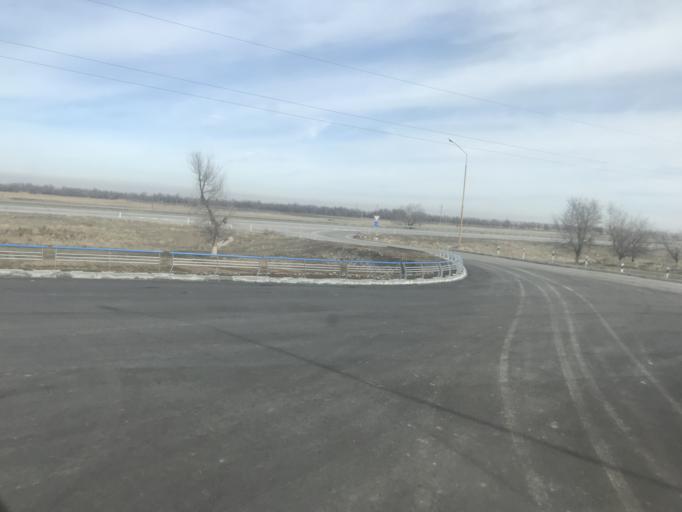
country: KZ
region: Zhambyl
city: Sarykemer
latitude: 43.0087
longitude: 71.7853
